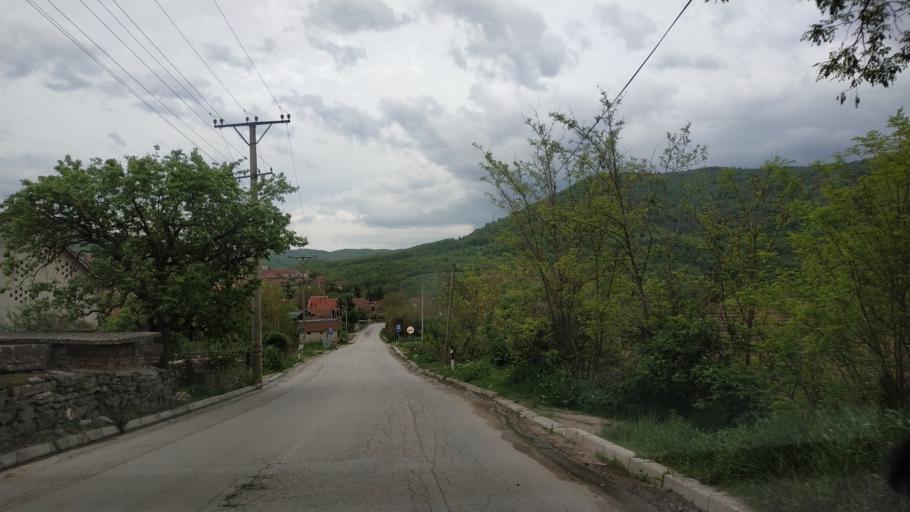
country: RS
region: Central Serbia
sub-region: Nisavski Okrug
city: Aleksinac
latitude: 43.6360
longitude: 21.7169
